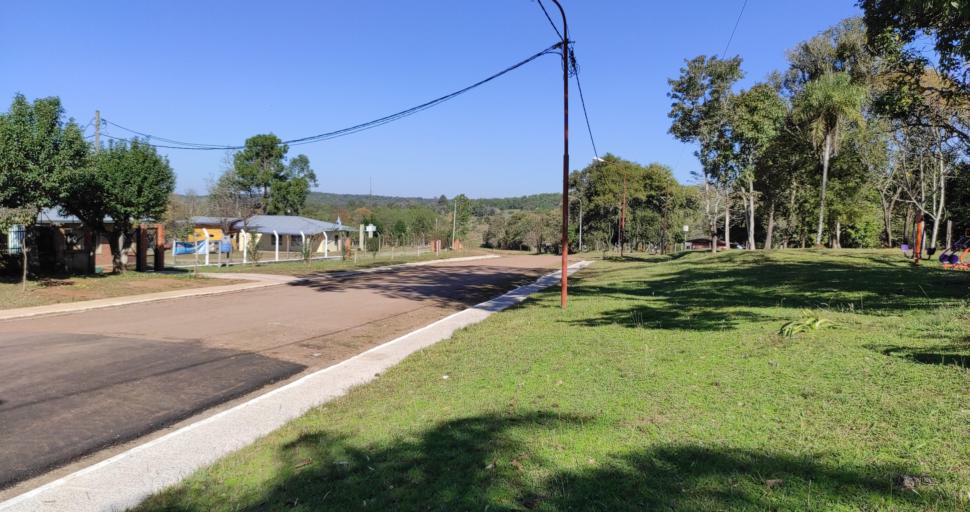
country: AR
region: Misiones
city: Cerro Cora
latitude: -27.6336
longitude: -55.7039
